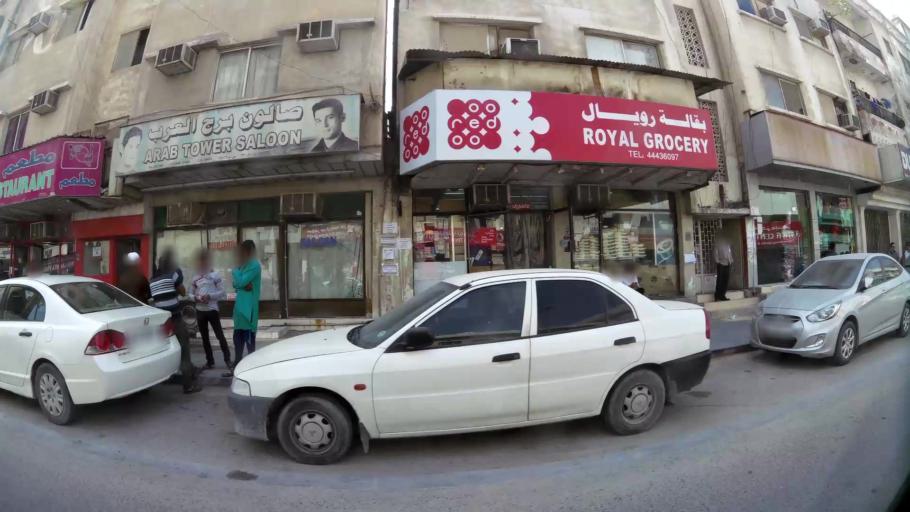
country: QA
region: Baladiyat ad Dawhah
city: Doha
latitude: 25.2810
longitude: 51.5288
